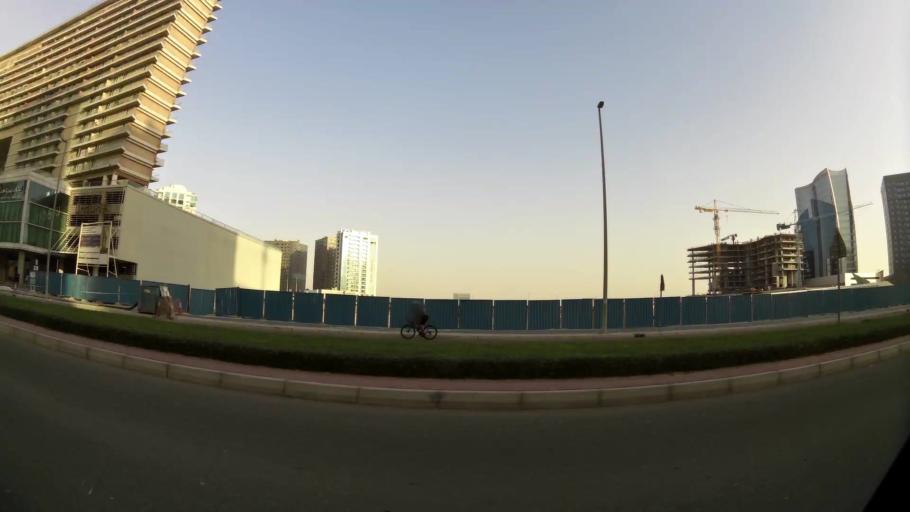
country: AE
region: Dubai
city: Dubai
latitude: 25.1804
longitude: 55.2691
